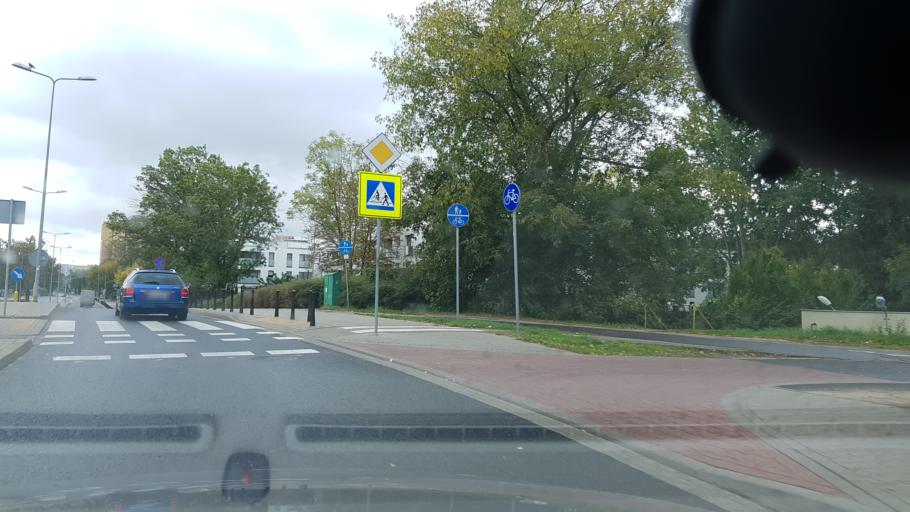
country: PL
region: Masovian Voivodeship
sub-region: Warszawa
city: Zoliborz
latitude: 52.2898
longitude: 20.9749
